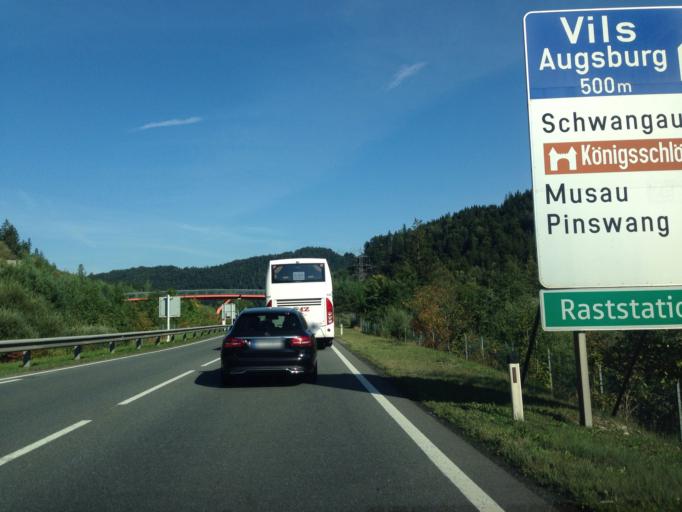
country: AT
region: Tyrol
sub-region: Politischer Bezirk Reutte
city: Musau
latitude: 47.5416
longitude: 10.6657
